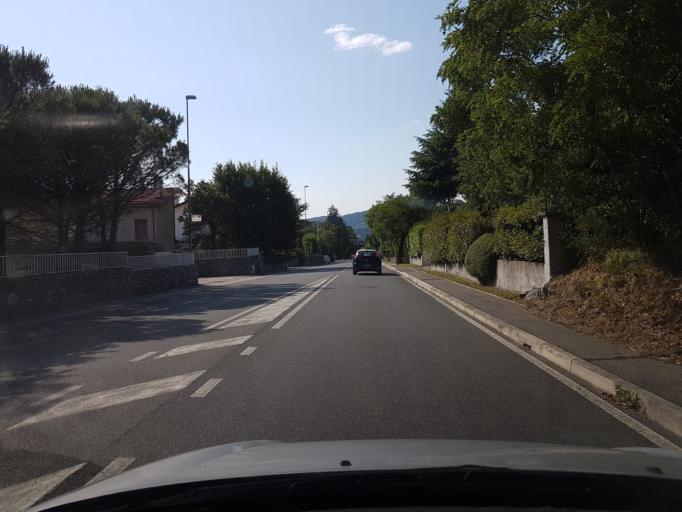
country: IT
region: Friuli Venezia Giulia
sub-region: Provincia di Trieste
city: Sistiana-Visogliano
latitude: 45.7643
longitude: 13.6481
